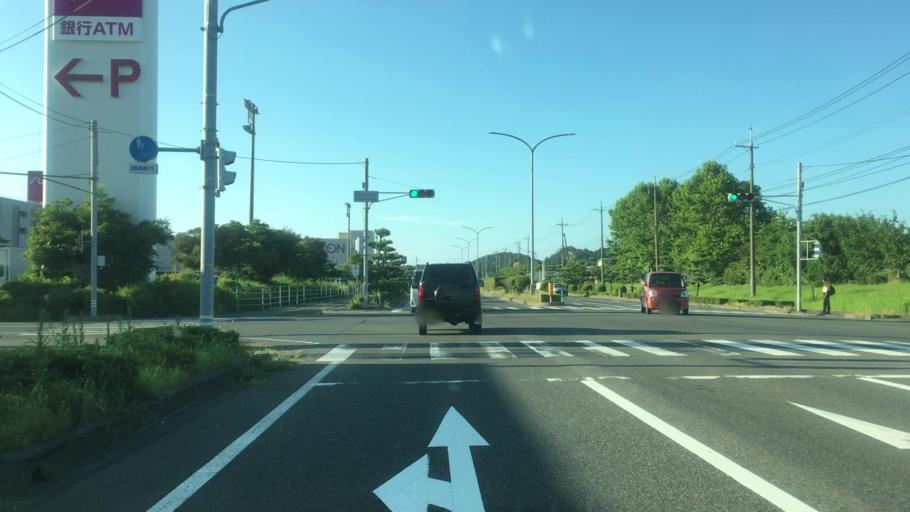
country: JP
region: Tottori
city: Tottori
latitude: 35.5222
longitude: 134.2025
